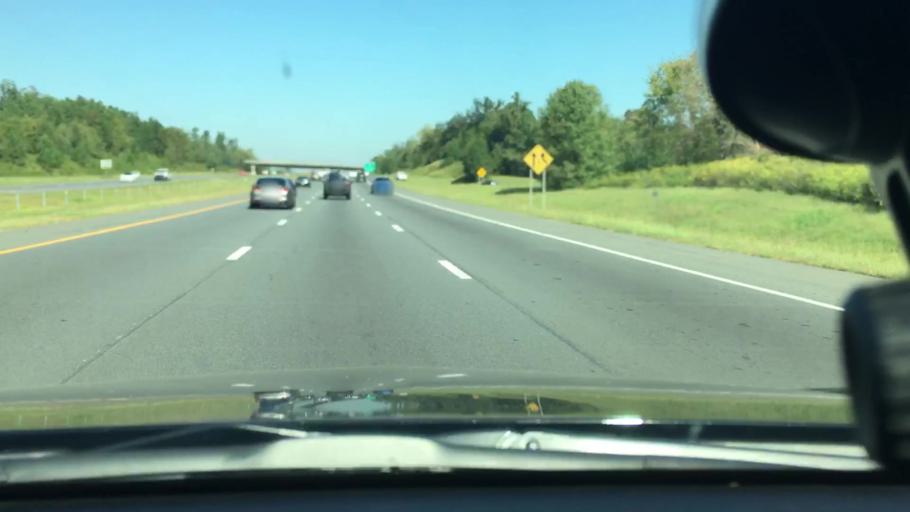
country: US
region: North Carolina
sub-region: Cabarrus County
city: Harrisburg
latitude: 35.3150
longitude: -80.7096
